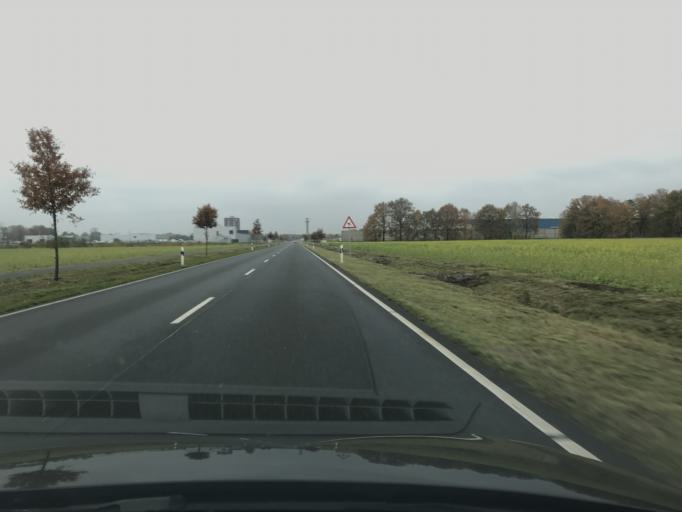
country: DE
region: North Rhine-Westphalia
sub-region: Regierungsbezirk Munster
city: Ladbergen
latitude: 52.1216
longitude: 7.6957
